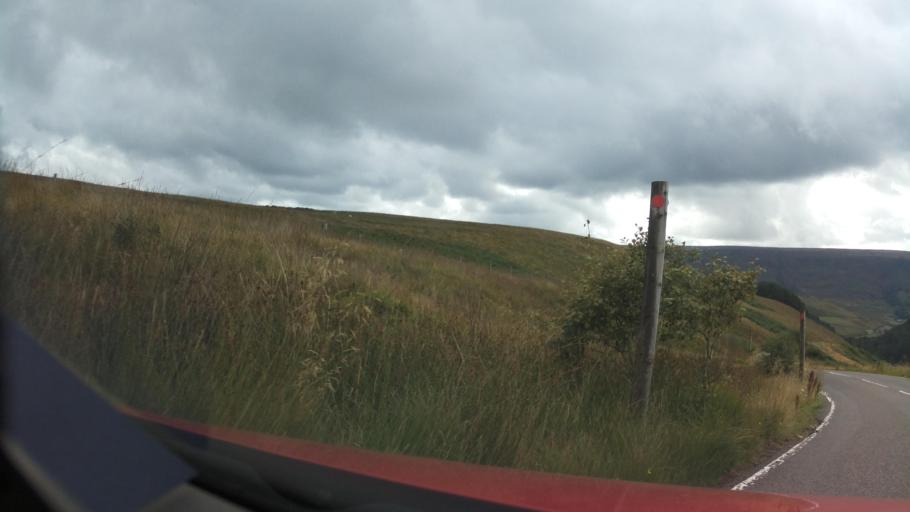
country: GB
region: England
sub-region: Kirklees
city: Meltham
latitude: 53.5135
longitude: -1.8531
